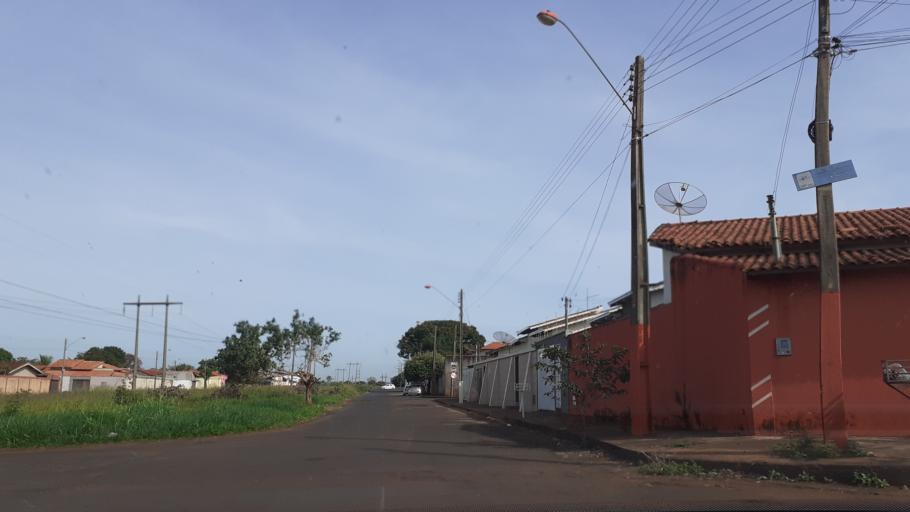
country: BR
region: Goias
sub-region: Itumbiara
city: Itumbiara
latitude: -18.4189
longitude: -49.2402
